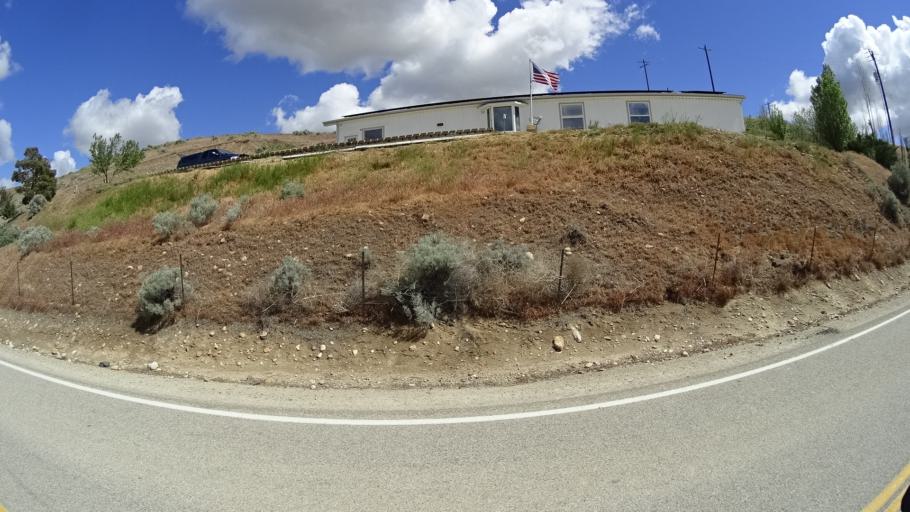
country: US
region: Idaho
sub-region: Ada County
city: Garden City
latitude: 43.4988
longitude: -116.2851
